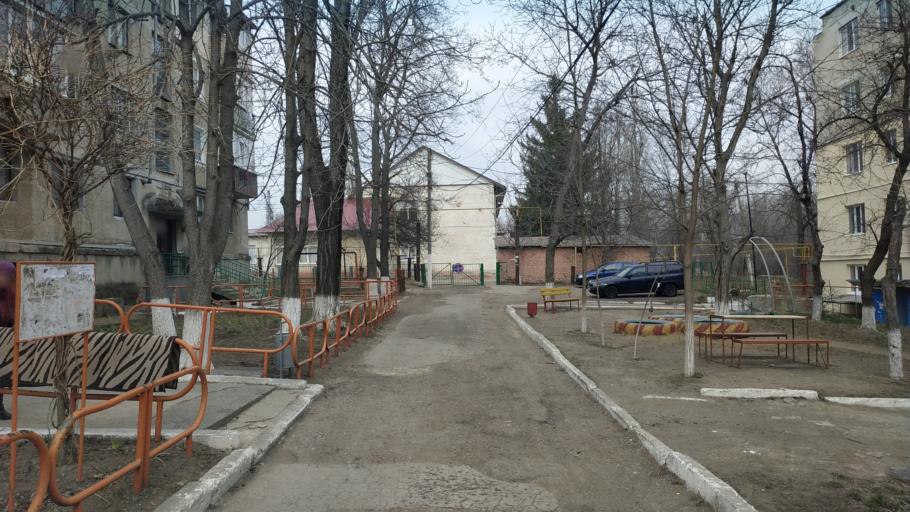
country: MD
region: Chisinau
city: Singera
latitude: 46.9357
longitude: 28.9786
